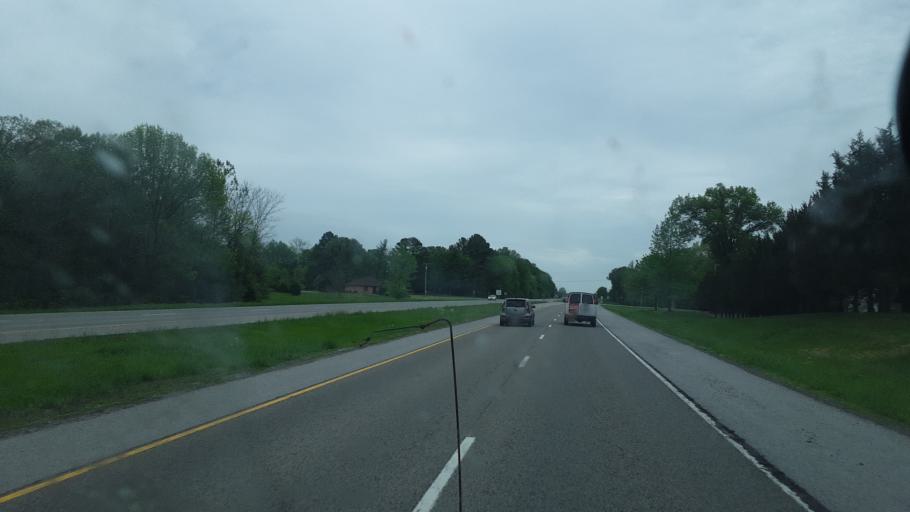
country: US
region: Illinois
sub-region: Jackson County
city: Carbondale
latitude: 37.7474
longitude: -89.2607
